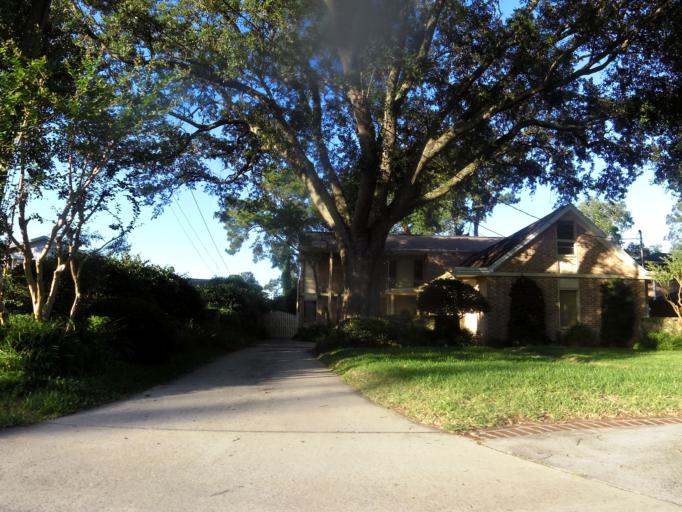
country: US
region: Florida
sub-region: Clay County
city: Orange Park
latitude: 30.2524
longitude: -81.6934
